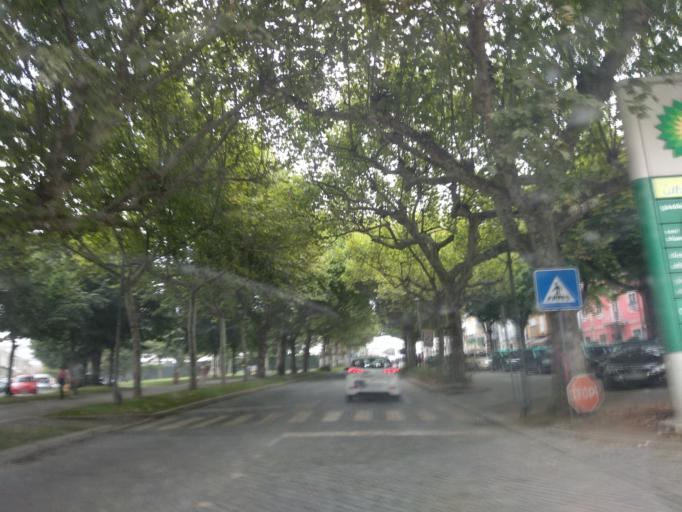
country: PT
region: Braga
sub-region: Vila Verde
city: Vila Verde
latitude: 41.6510
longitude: -8.4350
